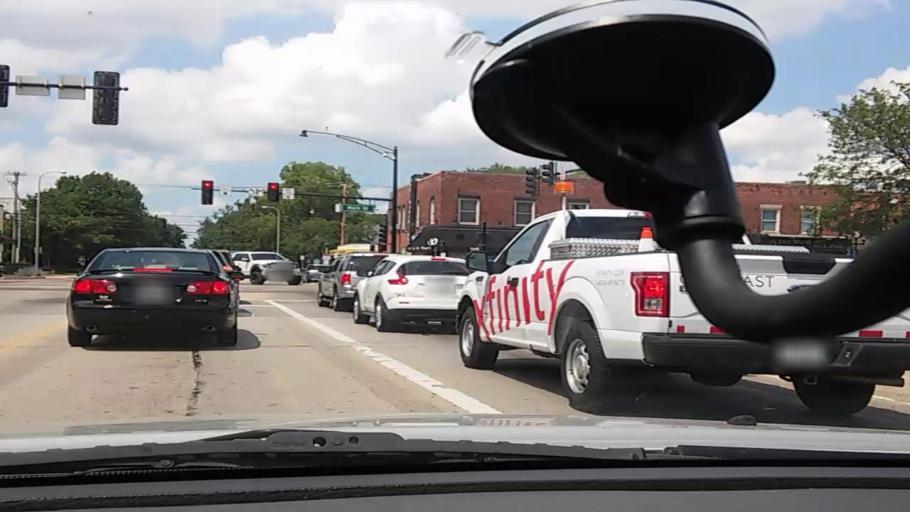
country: US
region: Illinois
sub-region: Peoria County
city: West Peoria
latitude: 40.6994
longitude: -89.6132
